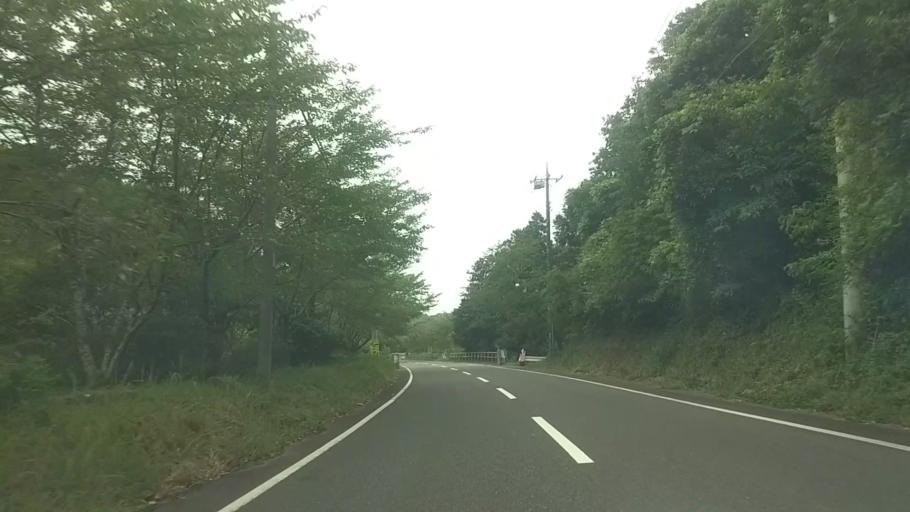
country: JP
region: Chiba
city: Kimitsu
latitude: 35.2242
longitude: 139.9530
